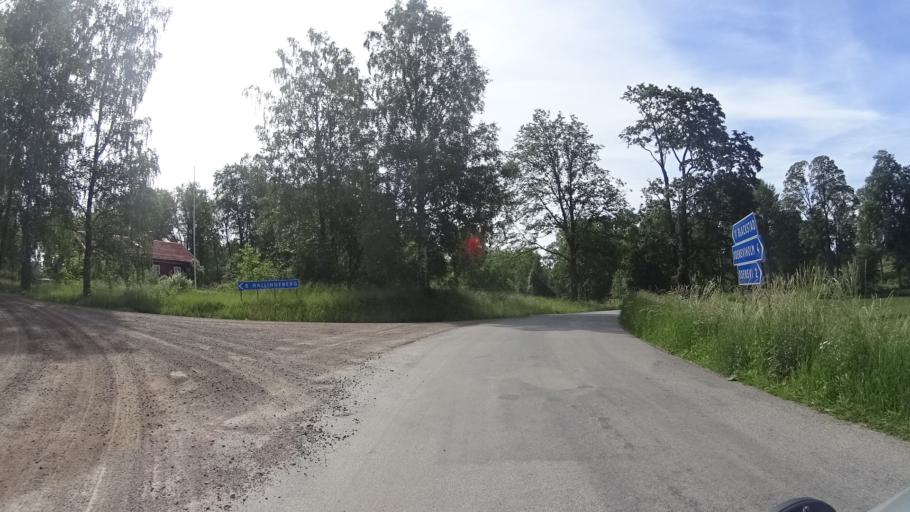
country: SE
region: Kalmar
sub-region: Vasterviks Kommun
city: Overum
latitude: 57.8731
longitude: 16.1762
